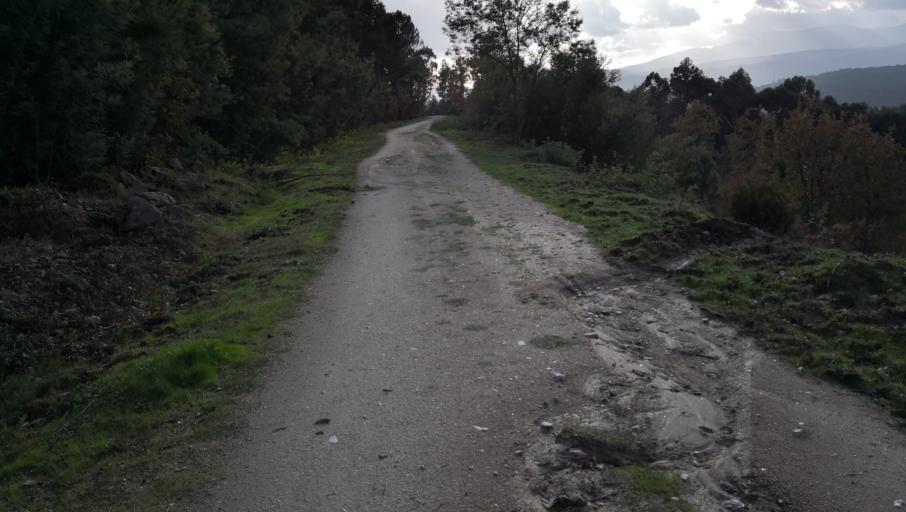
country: PT
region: Vila Real
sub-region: Vila Real
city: Vila Real
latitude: 41.3283
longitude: -7.7093
